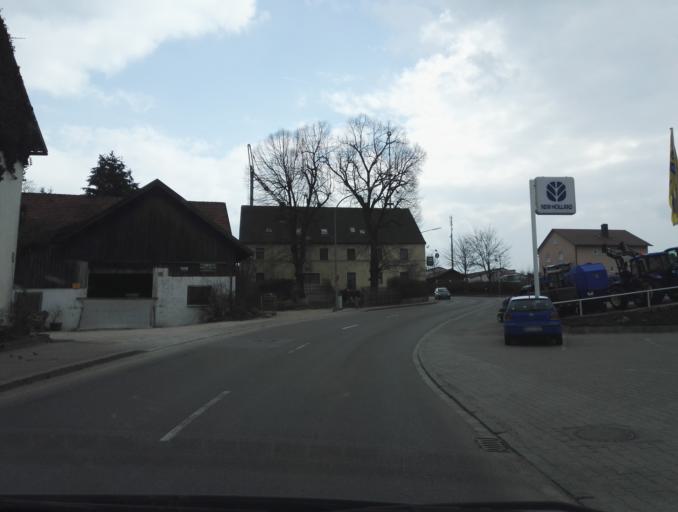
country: DE
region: Bavaria
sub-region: Lower Bavaria
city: Rottenburg an der Laaber
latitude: 48.7105
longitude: 12.0171
